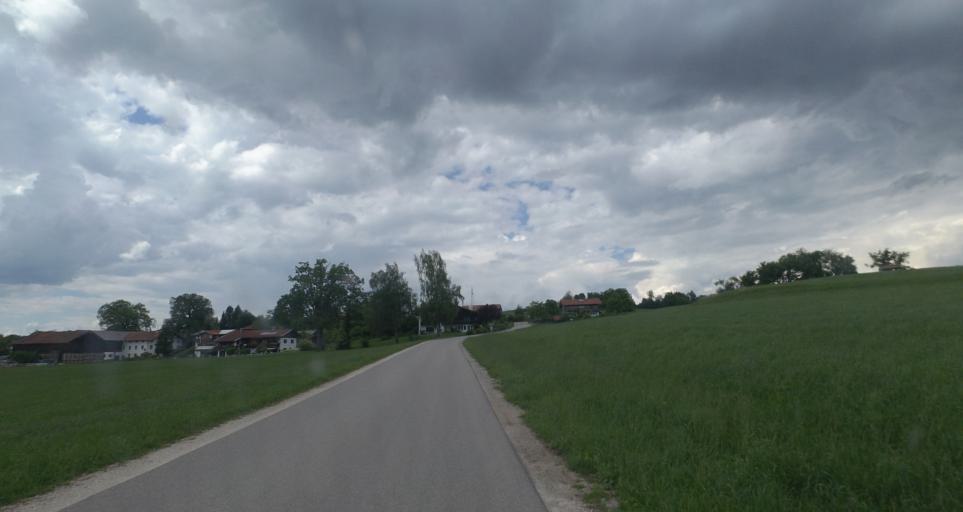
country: DE
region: Bavaria
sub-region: Upper Bavaria
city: Vachendorf
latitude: 47.8494
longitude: 12.5835
